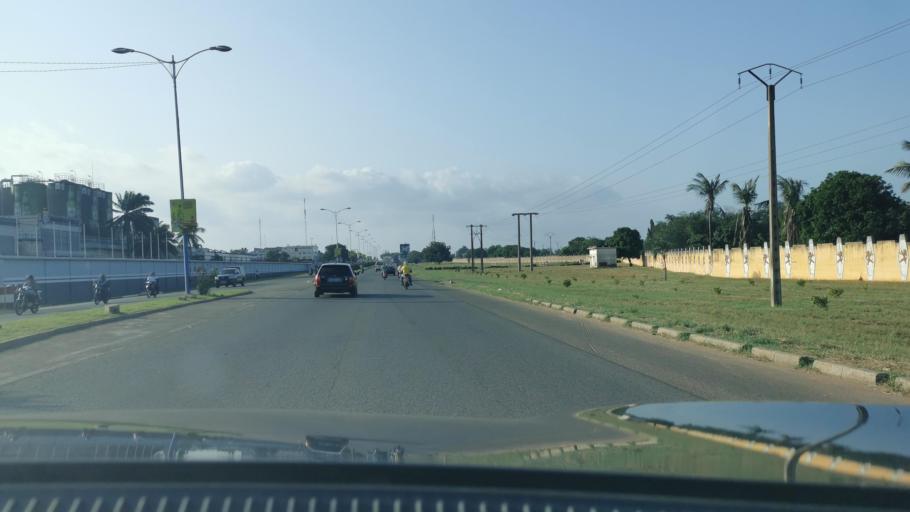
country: TG
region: Maritime
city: Lome
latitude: 6.2093
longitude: 1.2087
